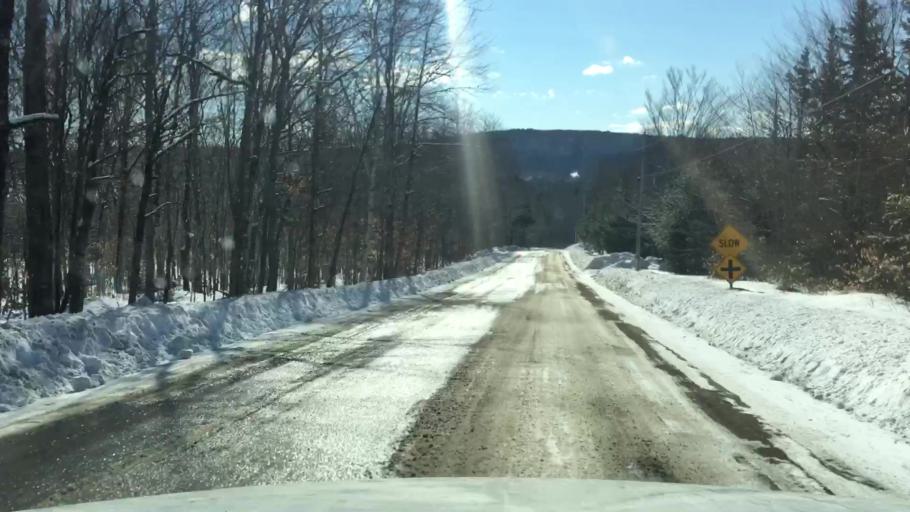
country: US
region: Maine
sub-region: Washington County
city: Calais
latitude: 45.0737
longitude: -67.5009
